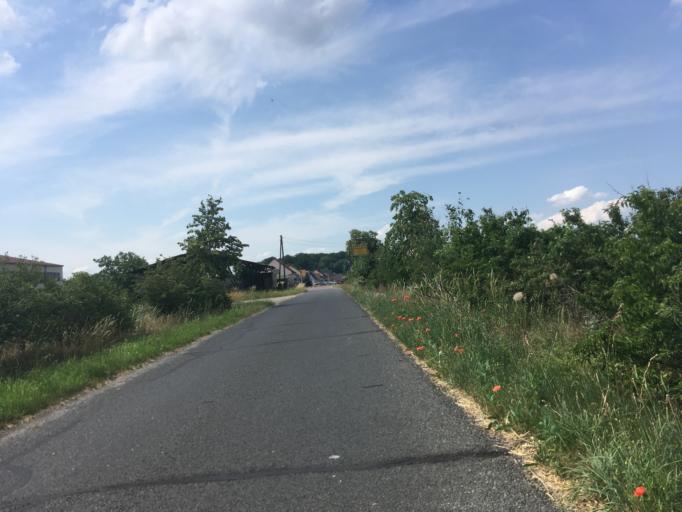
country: DE
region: Saxony-Anhalt
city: Quellendorf
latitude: 51.7760
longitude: 12.1150
